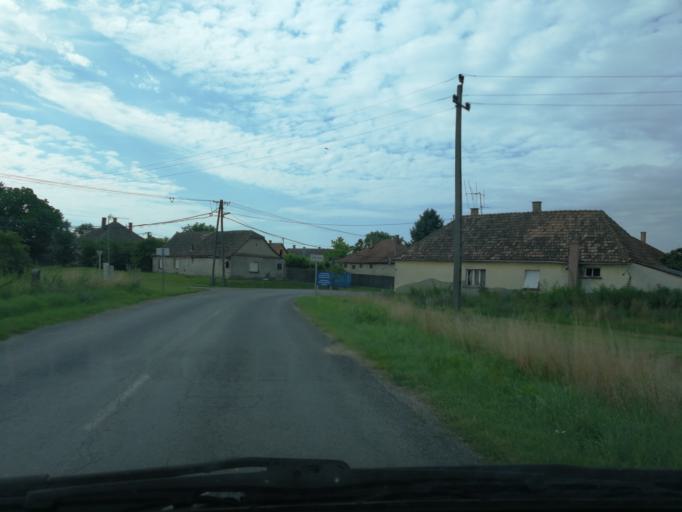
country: HU
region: Bacs-Kiskun
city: Batya
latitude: 46.4509
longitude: 19.0330
